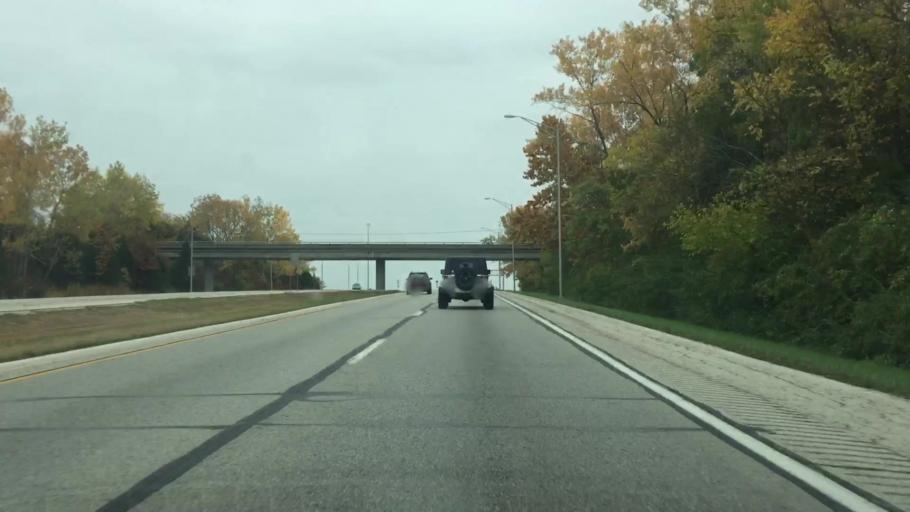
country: US
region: Kansas
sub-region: Wyandotte County
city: Edwardsville
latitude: 39.0104
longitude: -94.7942
